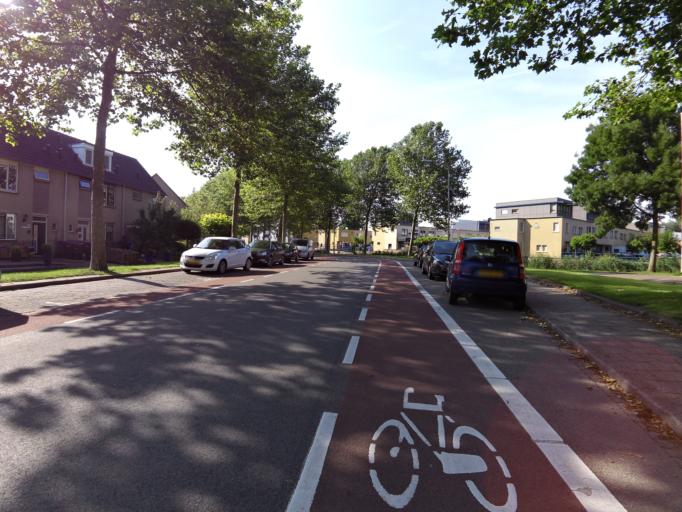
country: NL
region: South Holland
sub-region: Gemeente Sliedrecht
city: Sliedrecht
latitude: 51.8038
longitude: 4.7297
